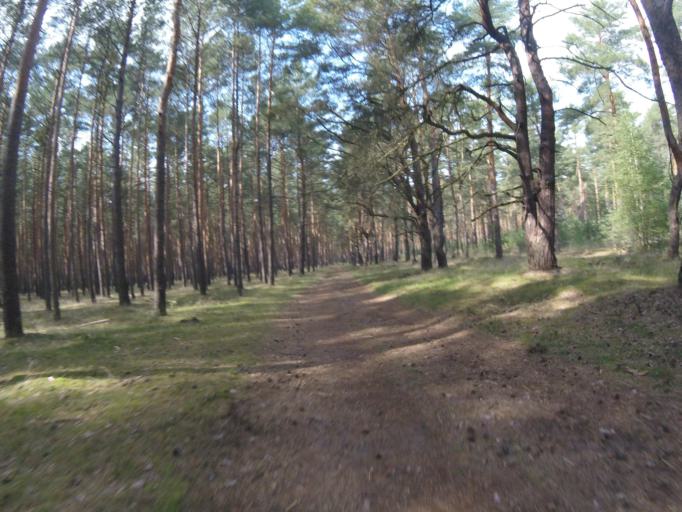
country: DE
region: Brandenburg
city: Bestensee
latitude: 52.2667
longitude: 13.6687
